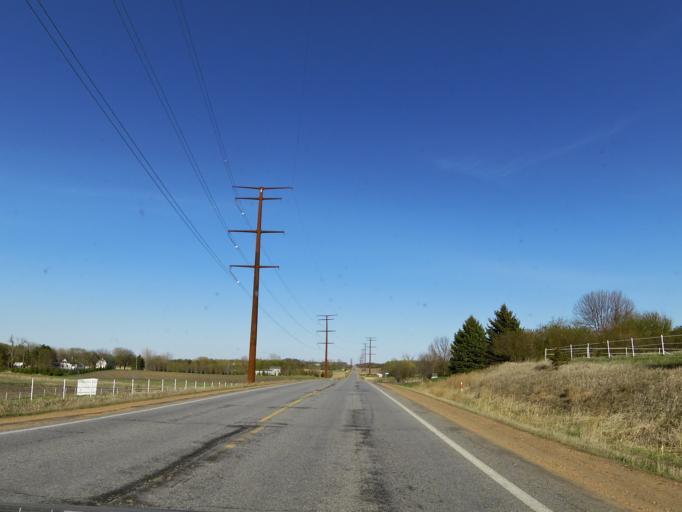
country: US
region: Minnesota
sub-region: Le Sueur County
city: New Prague
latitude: 44.5725
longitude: -93.4909
